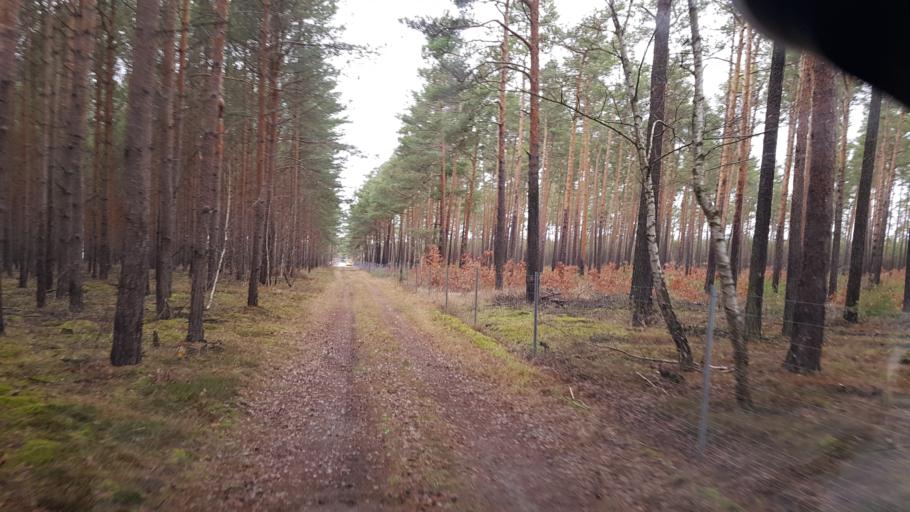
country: DE
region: Brandenburg
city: Altdobern
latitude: 51.6785
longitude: 14.0250
